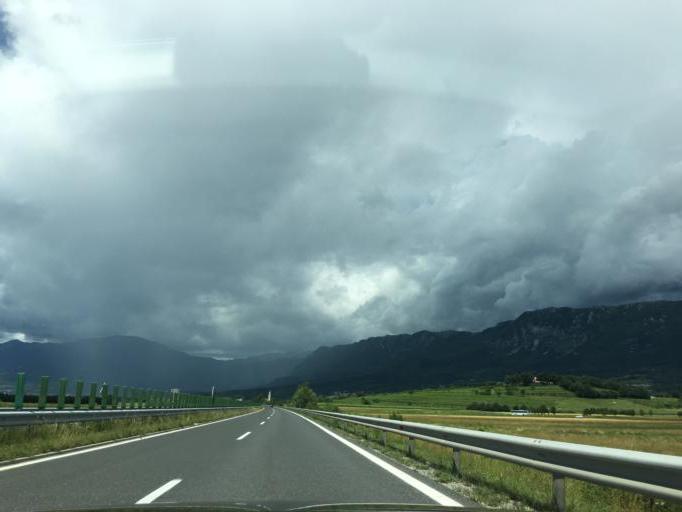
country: SI
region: Vipava
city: Vipava
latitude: 45.8476
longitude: 13.9492
